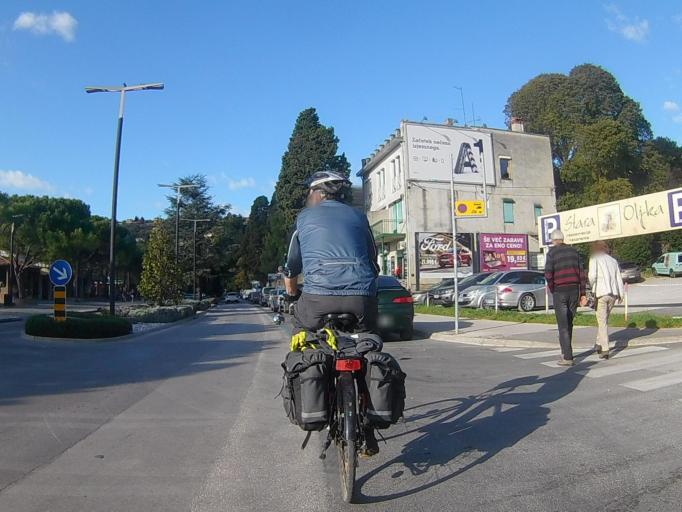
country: SI
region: Piran-Pirano
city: Portoroz
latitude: 45.5119
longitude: 13.5954
